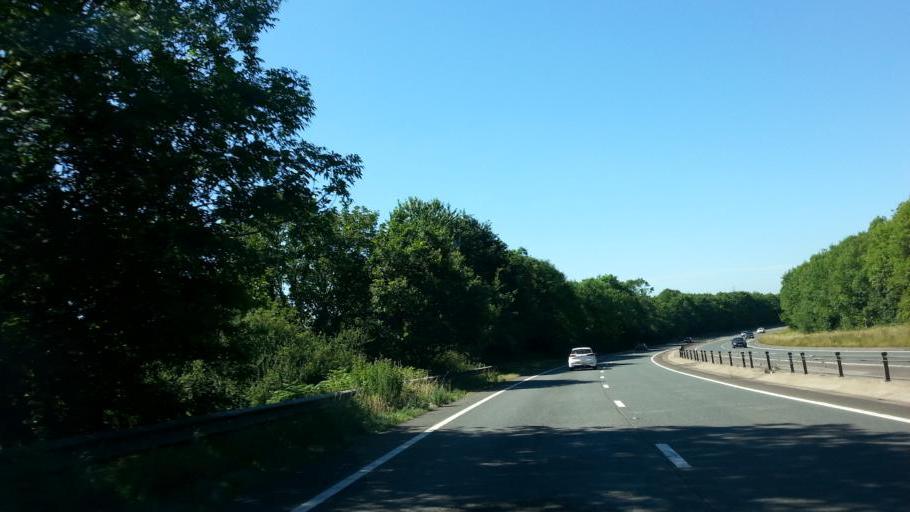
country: GB
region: Wales
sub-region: Newport
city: Langstone
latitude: 51.6090
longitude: -2.9133
